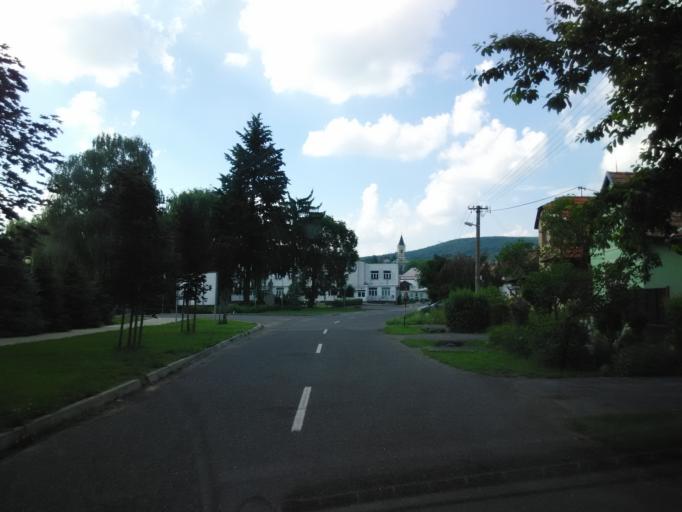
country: SK
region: Nitriansky
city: Tlmace
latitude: 48.2913
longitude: 18.5618
